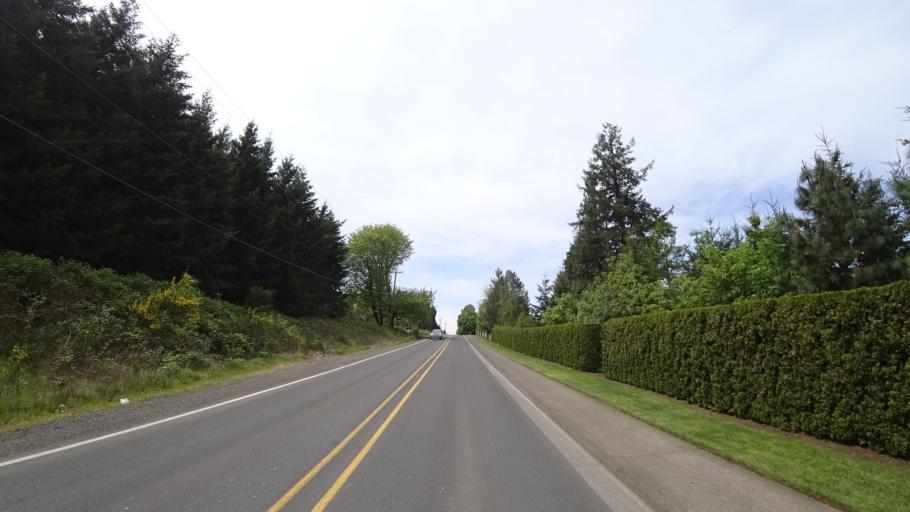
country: US
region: Oregon
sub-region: Washington County
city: Aloha
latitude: 45.4531
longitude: -122.8606
